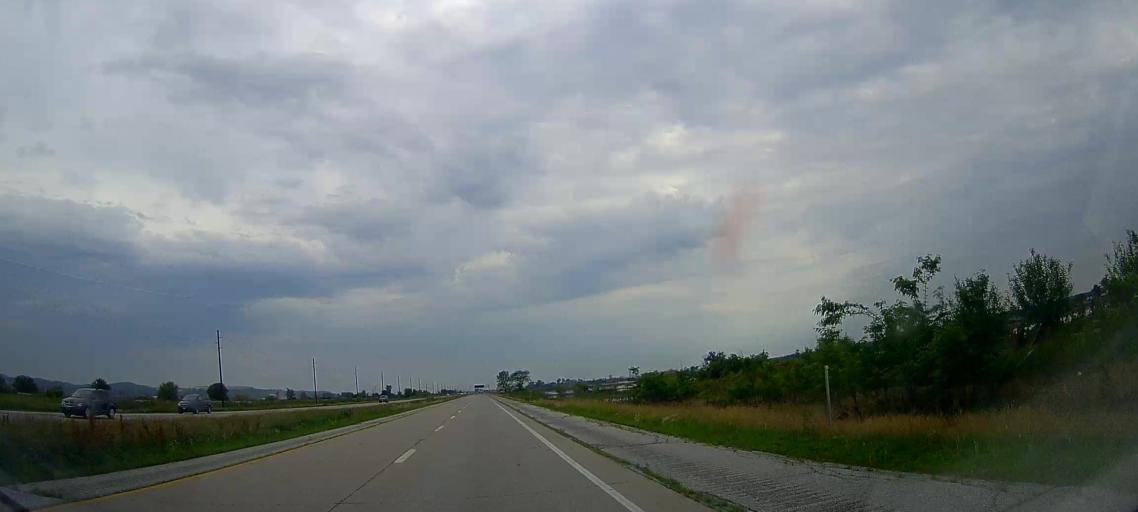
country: US
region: Iowa
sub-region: Pottawattamie County
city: Carter Lake
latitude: 41.3891
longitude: -95.8997
